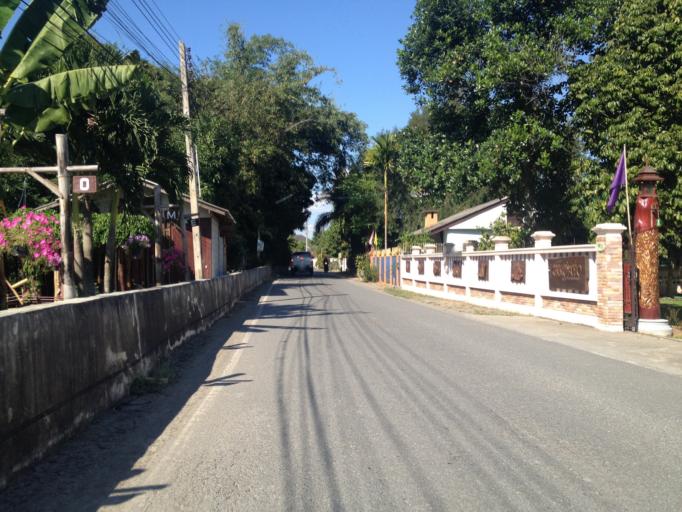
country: TH
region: Chiang Mai
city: Saraphi
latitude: 18.6978
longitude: 98.9871
